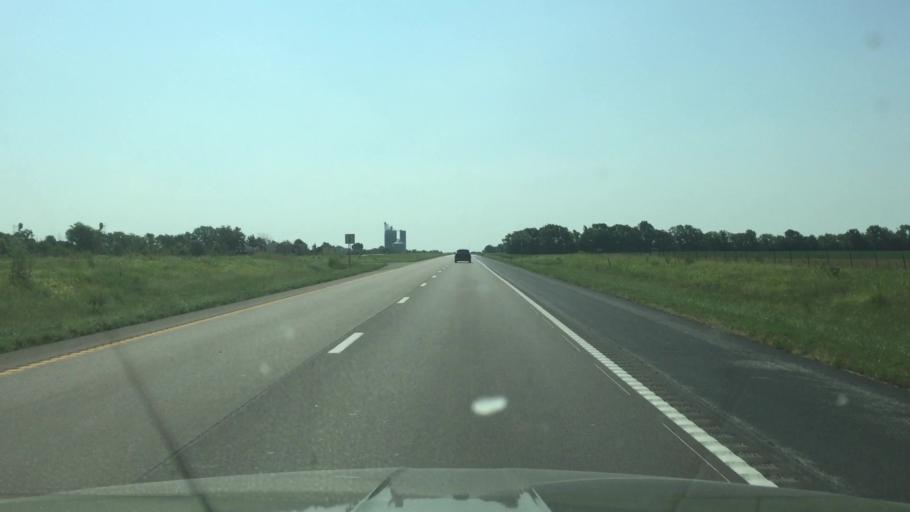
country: US
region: Missouri
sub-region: Pettis County
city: La Monte
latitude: 38.7567
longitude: -93.3649
